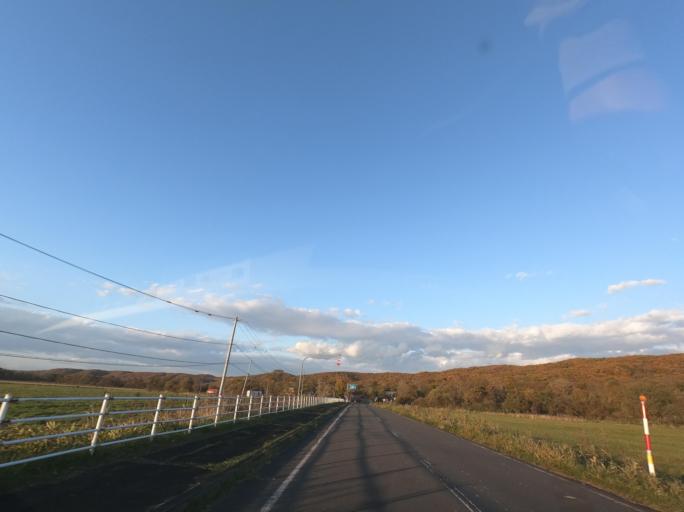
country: JP
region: Hokkaido
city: Kushiro
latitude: 43.2239
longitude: 144.4337
